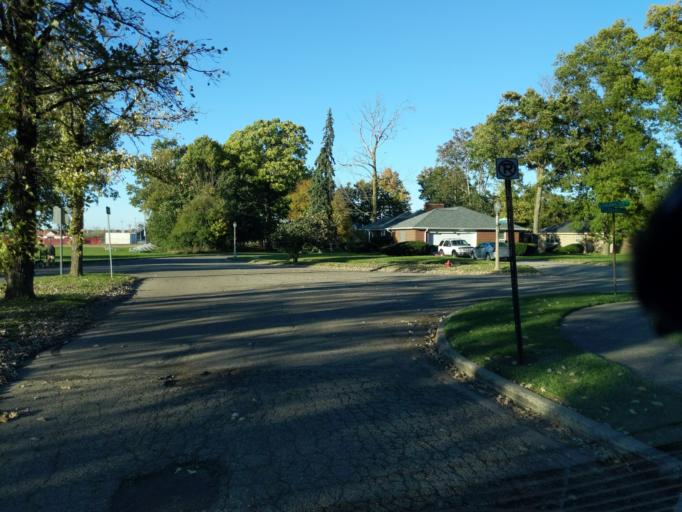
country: US
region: Michigan
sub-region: Ingham County
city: Edgemont Park
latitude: 42.7300
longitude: -84.5796
